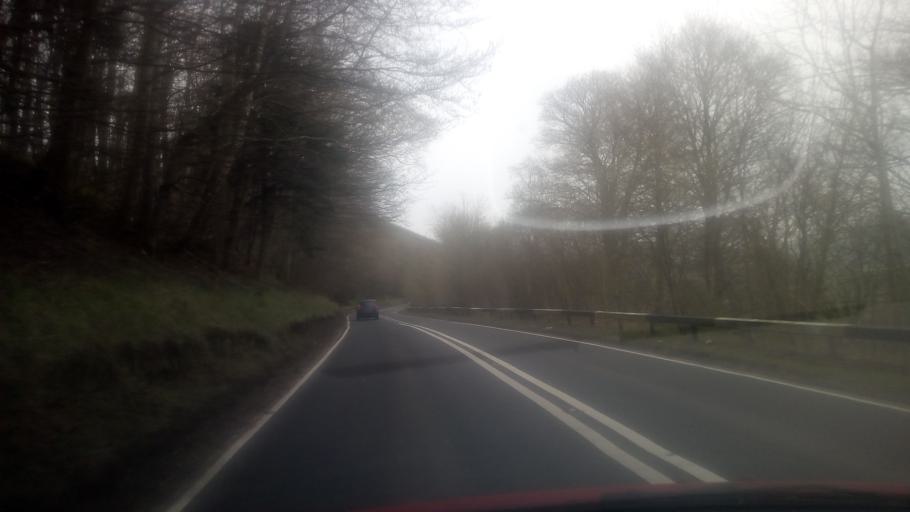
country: GB
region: Scotland
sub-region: The Scottish Borders
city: Galashiels
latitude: 55.6768
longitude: -2.8656
